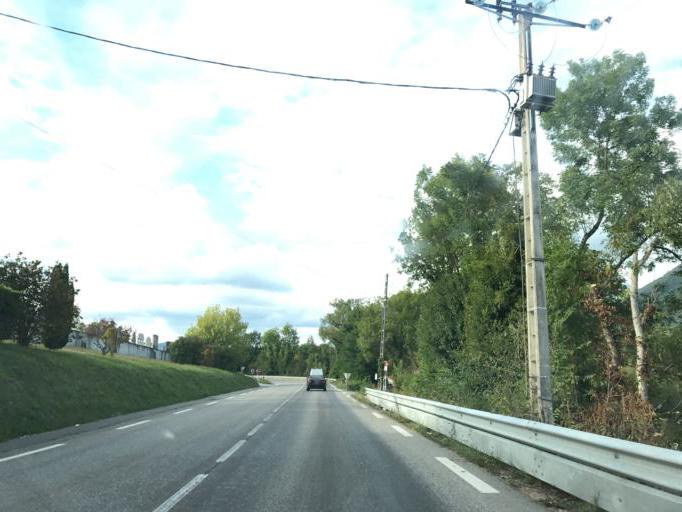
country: FR
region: Rhone-Alpes
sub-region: Departement de l'Ain
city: Bellegarde-sur-Valserine
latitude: 46.1186
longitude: 5.8232
